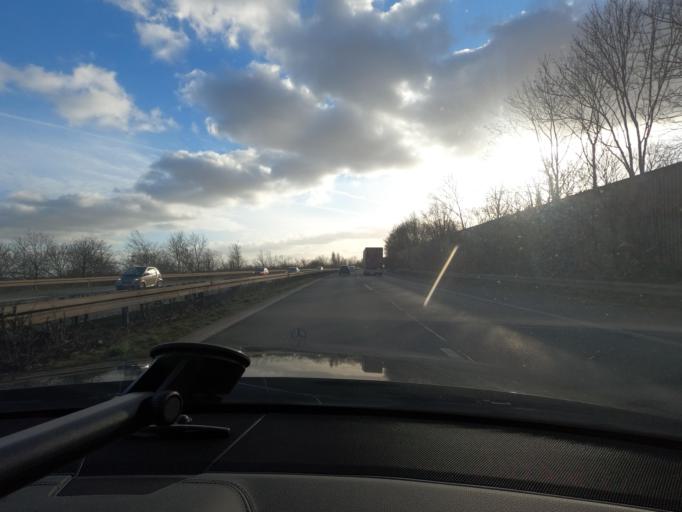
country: DE
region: North Rhine-Westphalia
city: Lanstrop
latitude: 51.5521
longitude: 7.5160
